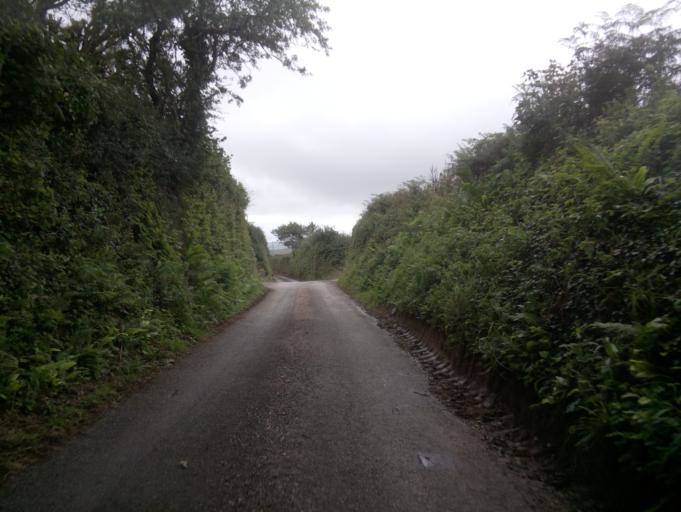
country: GB
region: England
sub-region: Devon
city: Kingsbridge
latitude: 50.2956
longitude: -3.7169
